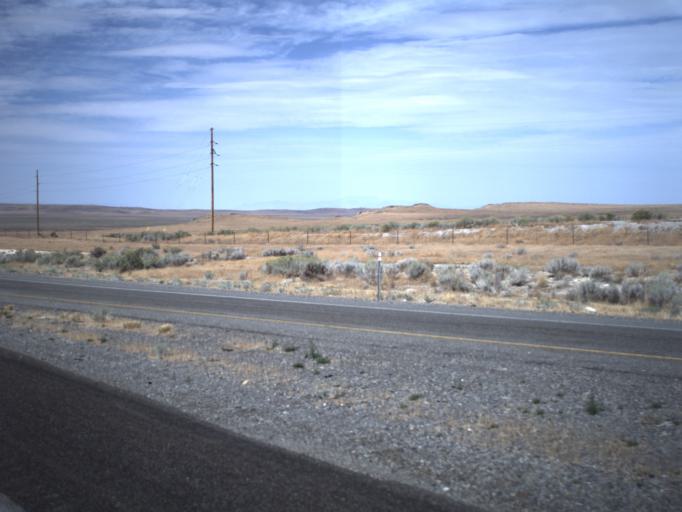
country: US
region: Utah
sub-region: Tooele County
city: Grantsville
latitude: 40.7601
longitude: -113.0132
